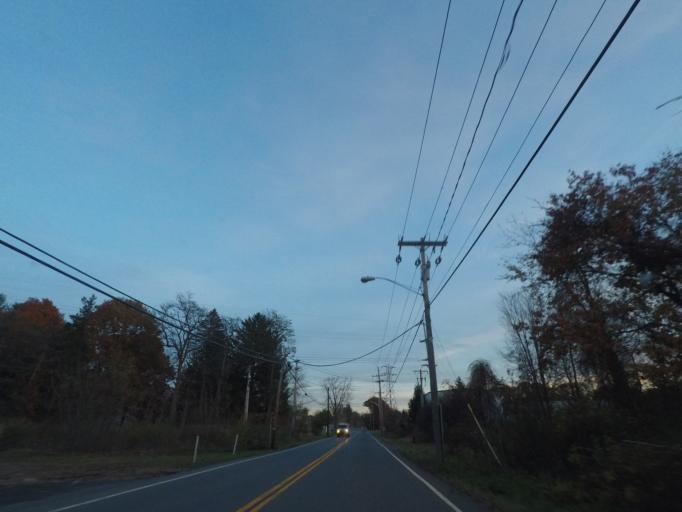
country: US
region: New York
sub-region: Schenectady County
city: Rotterdam
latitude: 42.7625
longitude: -73.9358
